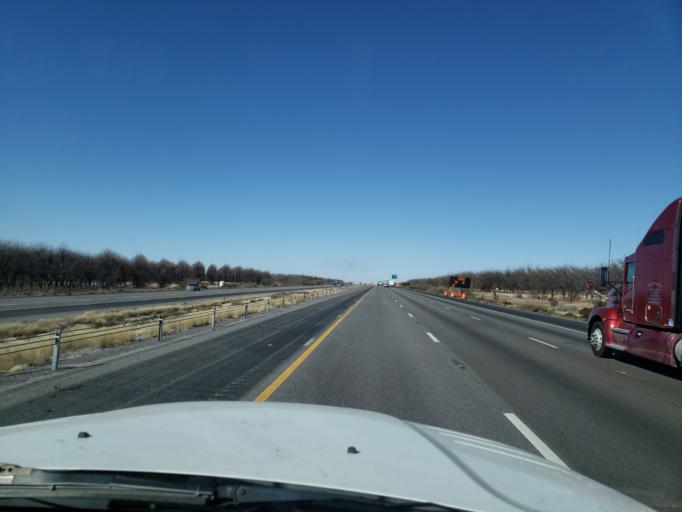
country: US
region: New Mexico
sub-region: Dona Ana County
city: University Park
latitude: 32.2331
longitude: -106.7122
